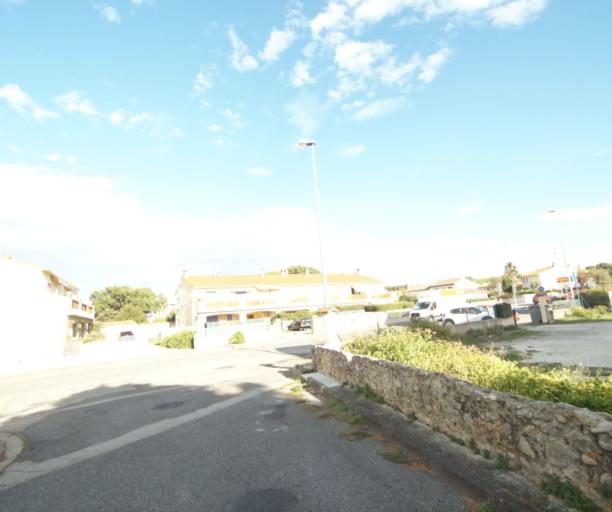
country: FR
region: Languedoc-Roussillon
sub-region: Departement des Pyrenees-Orientales
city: Argelers
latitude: 42.5476
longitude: 3.0332
